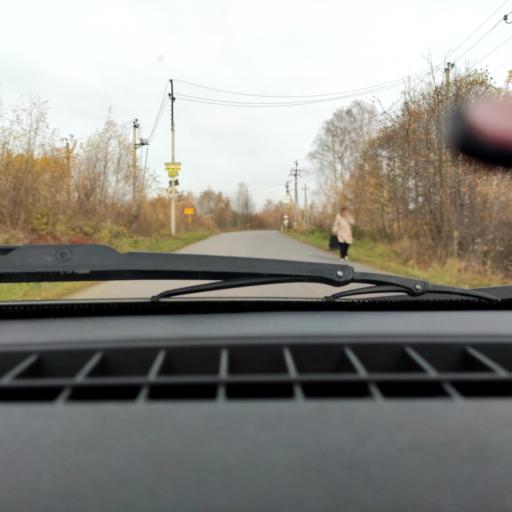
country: RU
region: Bashkortostan
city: Iglino
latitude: 54.8097
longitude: 56.1888
